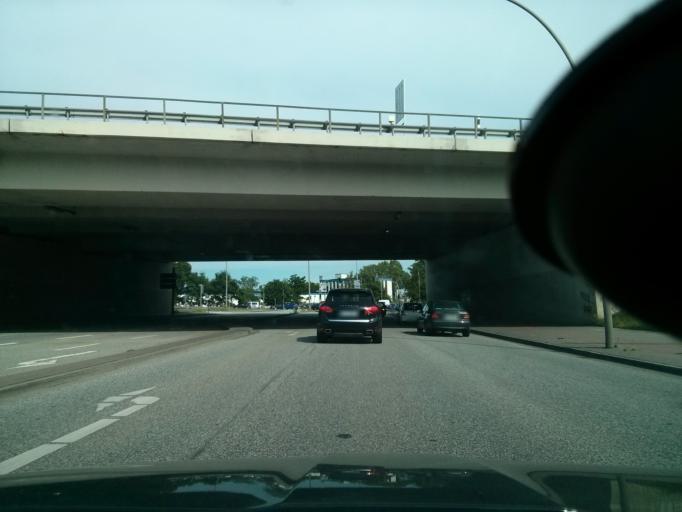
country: DE
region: Hamburg
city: Stellingen
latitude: 53.5826
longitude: 9.9149
